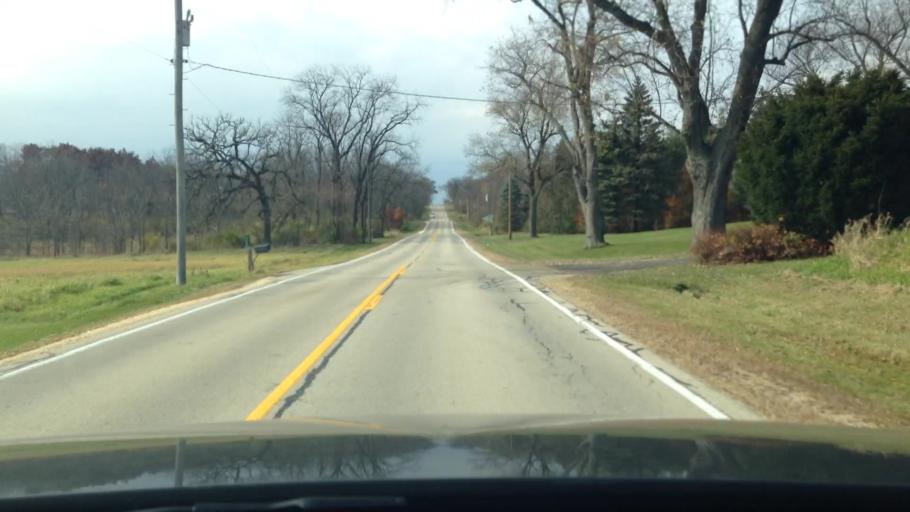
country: US
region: Illinois
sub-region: McHenry County
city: Woodstock
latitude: 42.2984
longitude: -88.4622
